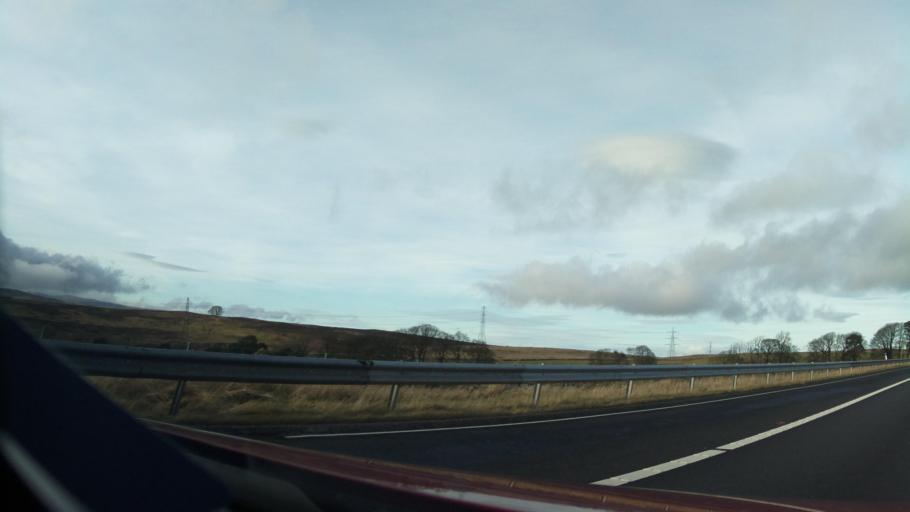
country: GB
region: England
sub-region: Cumbria
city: Appleby-in-Westmorland
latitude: 54.4940
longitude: -2.6452
